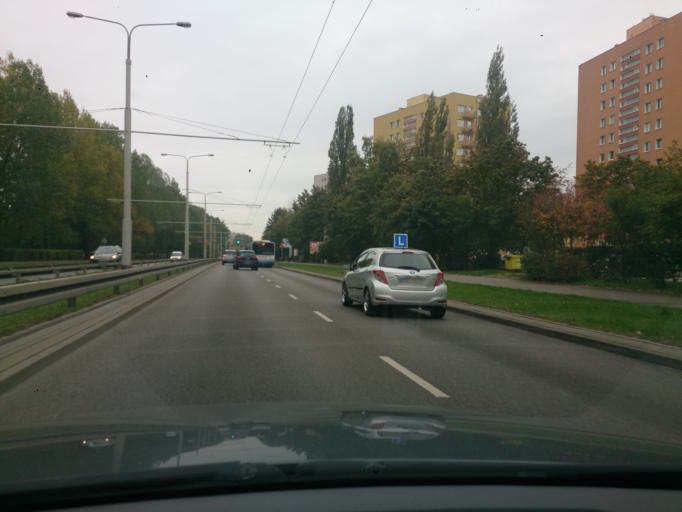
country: PL
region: Pomeranian Voivodeship
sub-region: Gdynia
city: Pogorze
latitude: 54.5406
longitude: 18.4647
